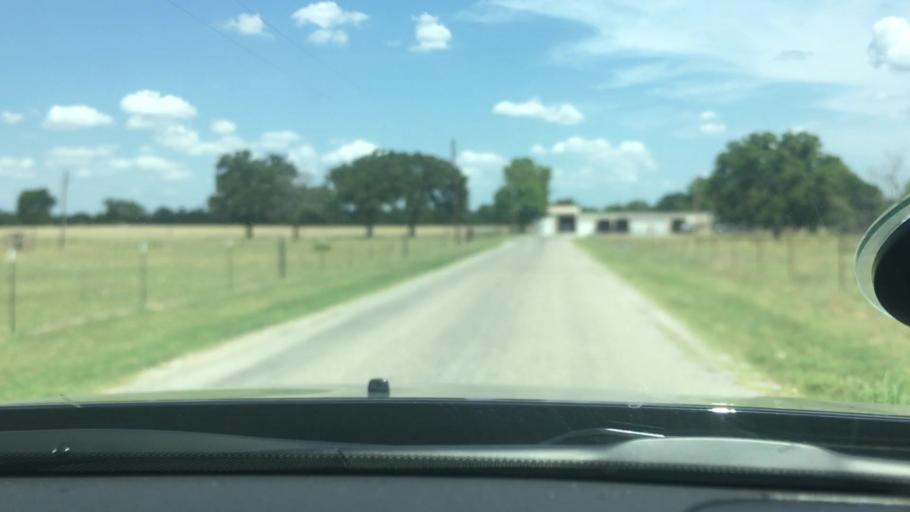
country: US
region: Oklahoma
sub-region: Carter County
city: Ardmore
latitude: 34.0695
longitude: -97.1957
